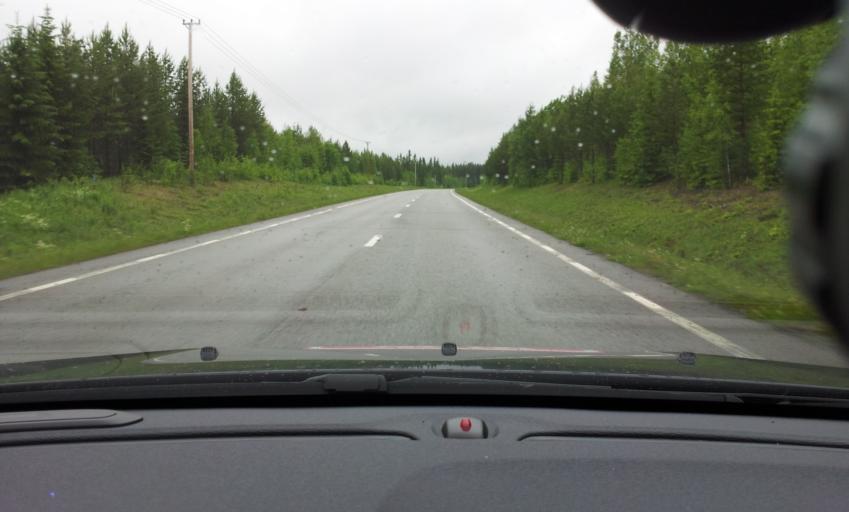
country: SE
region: Jaemtland
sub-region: Krokoms Kommun
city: Krokom
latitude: 63.4810
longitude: 14.5049
